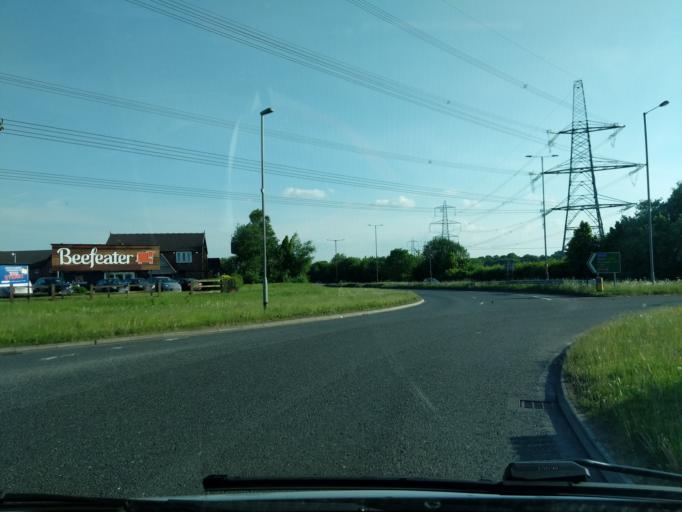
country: GB
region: England
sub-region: St. Helens
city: St Helens
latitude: 53.4186
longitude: -2.7452
